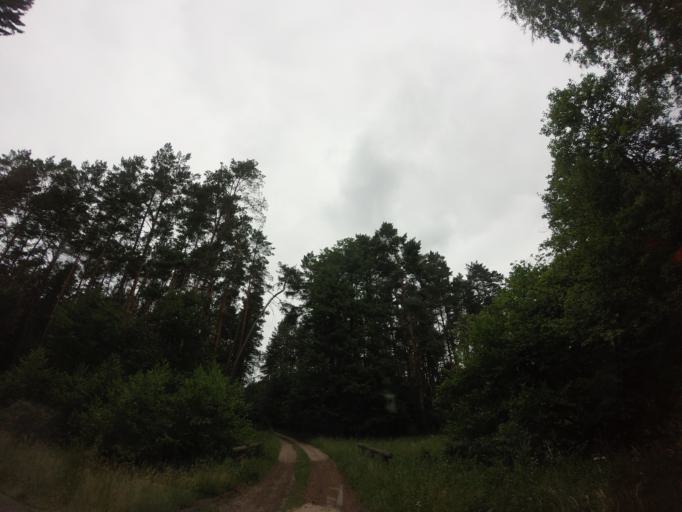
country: PL
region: Lubusz
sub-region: Powiat strzelecko-drezdenecki
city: Dobiegniew
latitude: 53.0888
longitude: 15.8479
